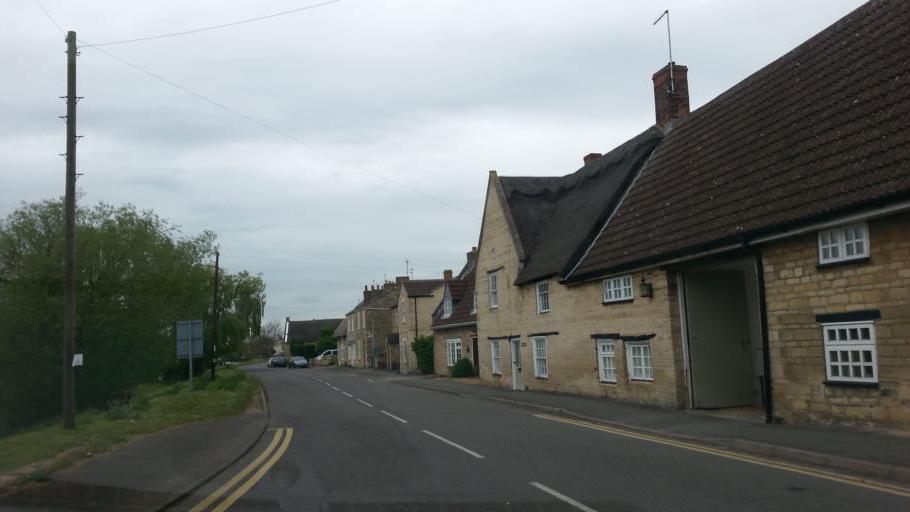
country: GB
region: England
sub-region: Peterborough
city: Northborough
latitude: 52.6712
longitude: -0.2997
